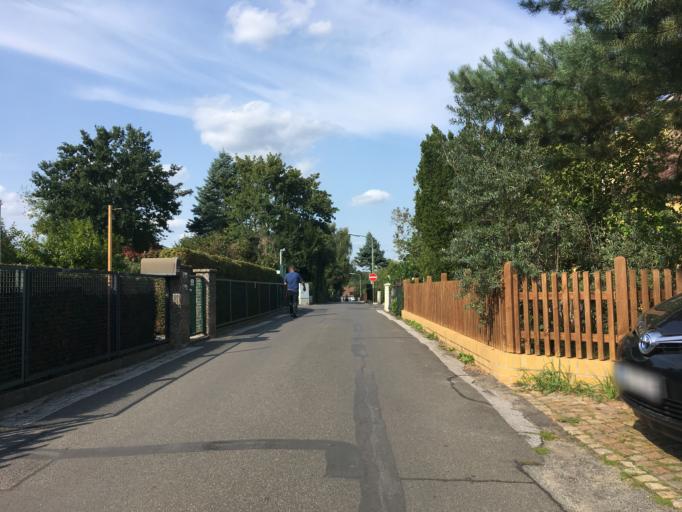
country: DE
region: Berlin
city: Lubars
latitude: 52.6200
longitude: 13.3388
